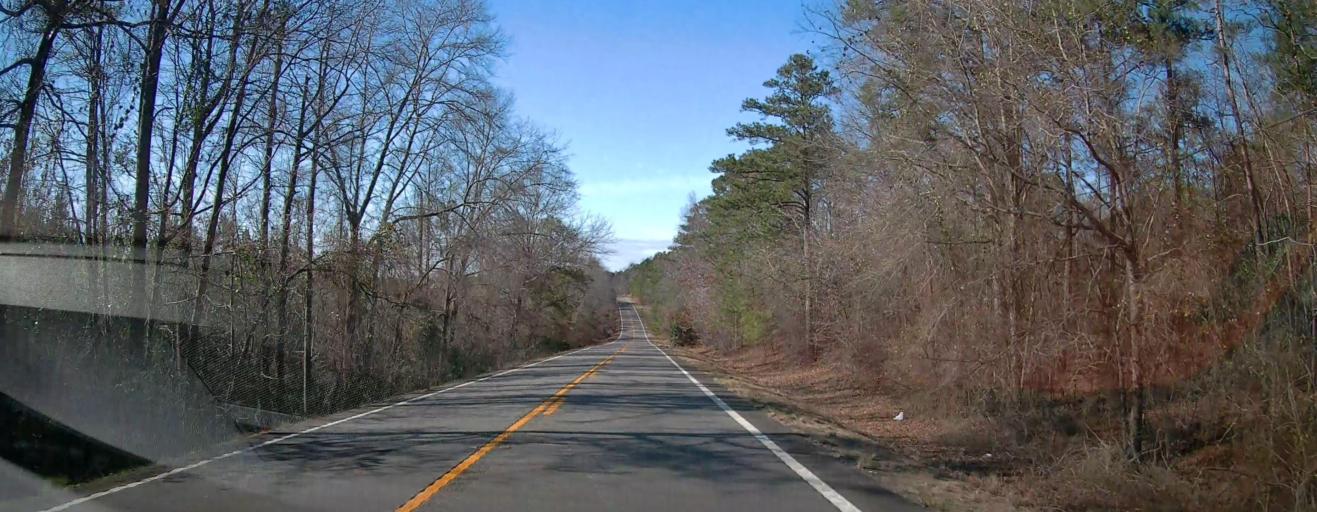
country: US
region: Georgia
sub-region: Macon County
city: Oglethorpe
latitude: 32.3612
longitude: -84.1807
